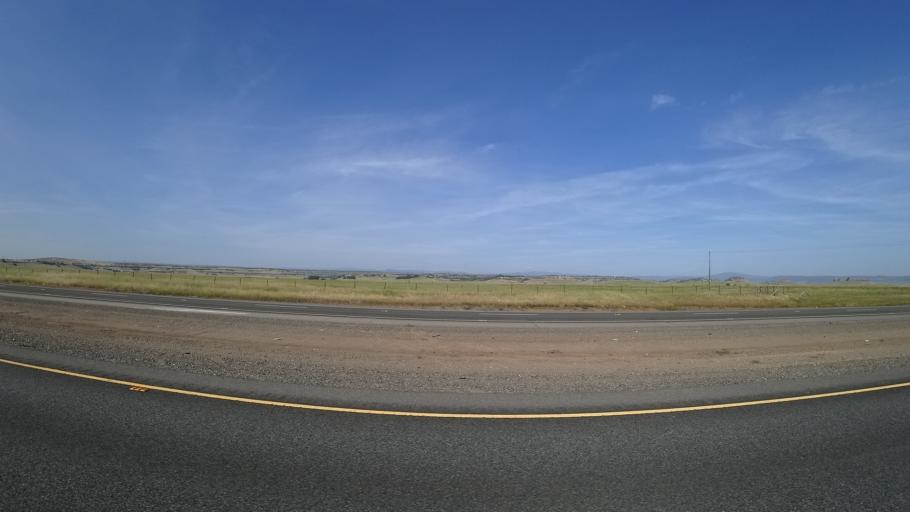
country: US
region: California
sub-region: Butte County
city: Durham
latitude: 39.6480
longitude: -121.7228
